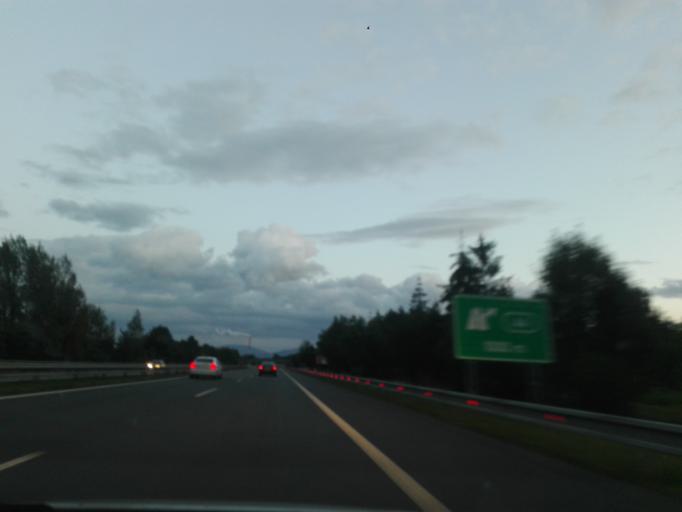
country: CZ
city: Paskov
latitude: 49.7406
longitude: 18.2806
